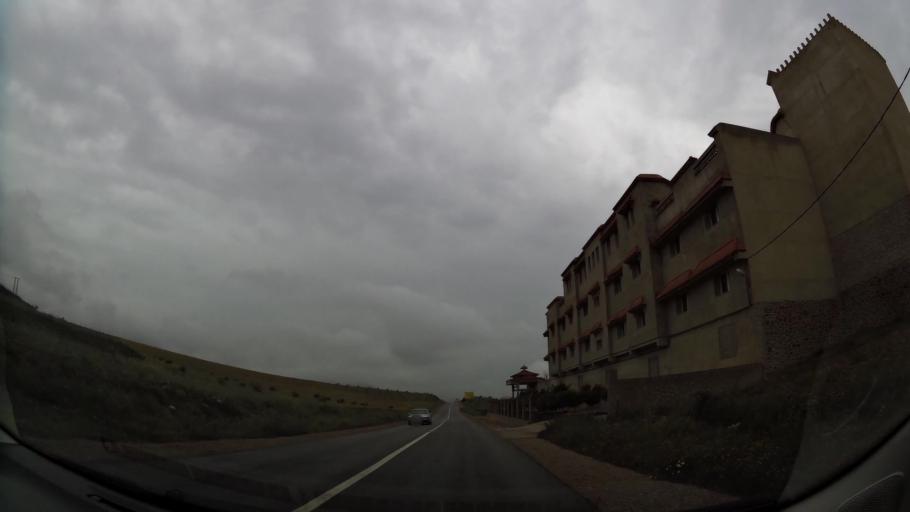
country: MA
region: Oriental
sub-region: Nador
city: Nador
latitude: 35.1525
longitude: -3.0354
